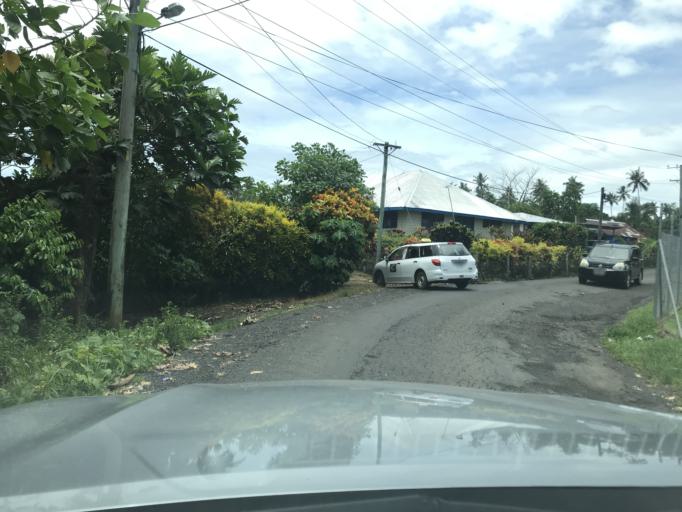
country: WS
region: Tuamasaga
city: Afenga
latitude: -13.8035
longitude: -171.8879
